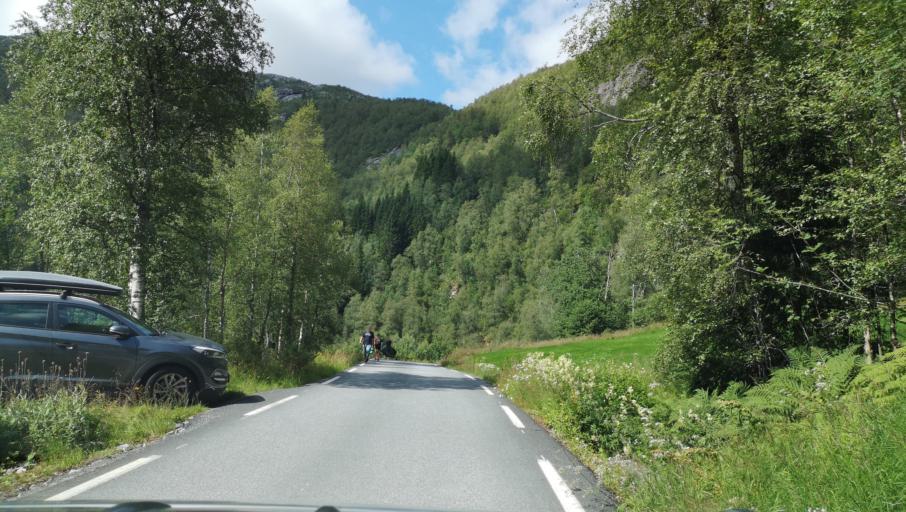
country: NO
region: Hordaland
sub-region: Modalen
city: Mo
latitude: 60.7845
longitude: 5.9415
